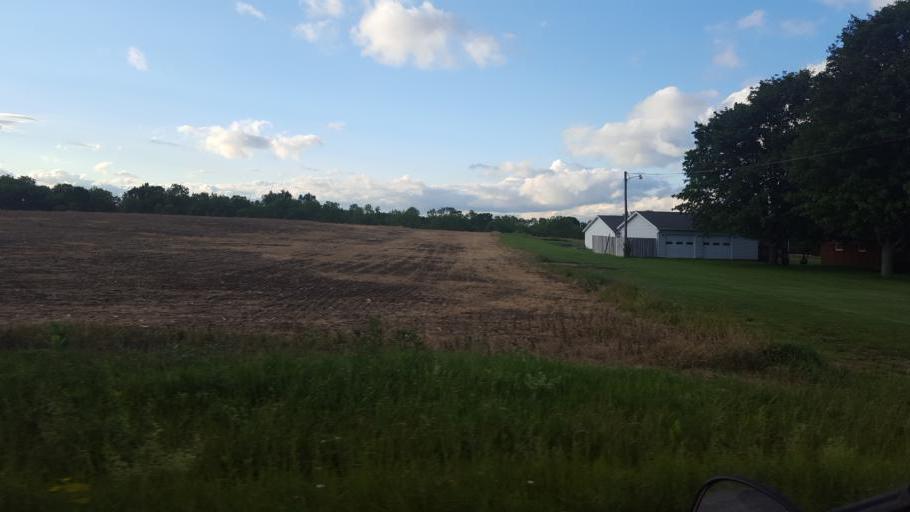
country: US
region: Ohio
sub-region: Knox County
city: Mount Vernon
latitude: 40.3854
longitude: -82.5183
